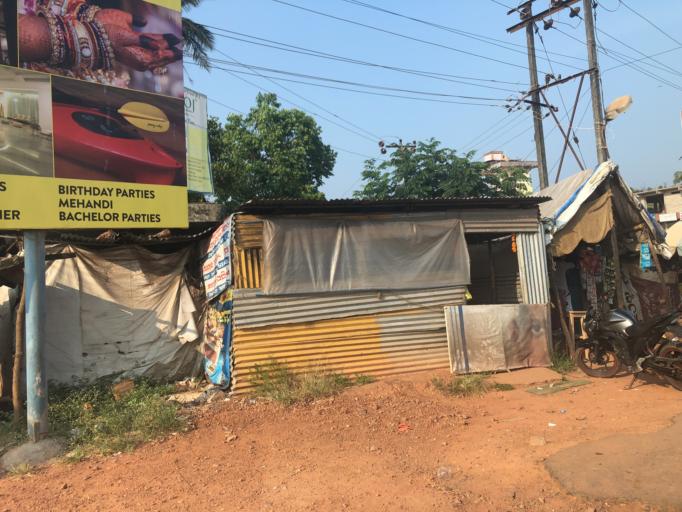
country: IN
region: Karnataka
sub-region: Dakshina Kannada
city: Ullal
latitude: 12.8146
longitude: 74.8582
